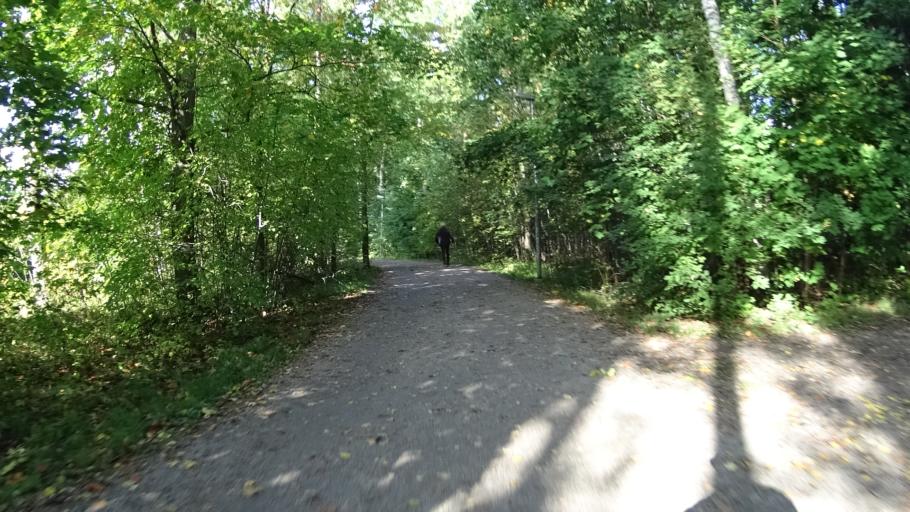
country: FI
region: Uusimaa
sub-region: Helsinki
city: Teekkarikylae
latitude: 60.2130
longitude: 24.8704
